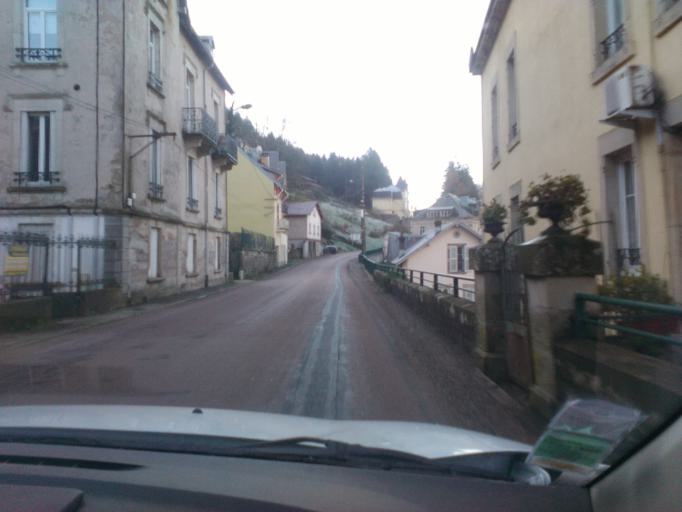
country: FR
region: Lorraine
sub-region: Departement des Vosges
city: Plombieres-les-Bains
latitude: 47.9640
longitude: 6.4589
